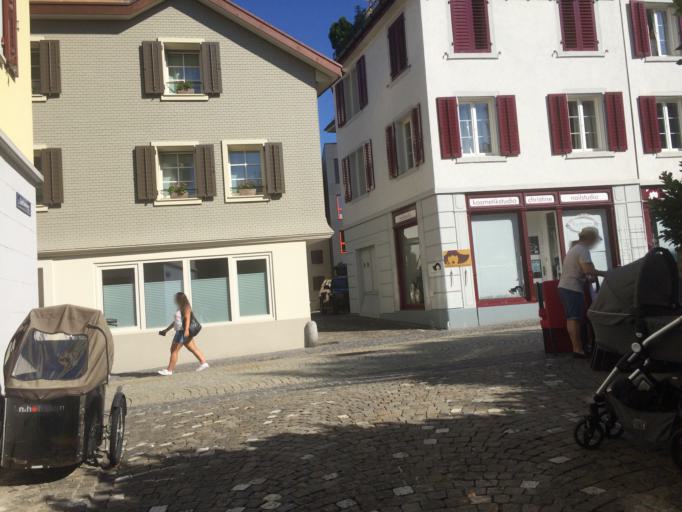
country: CH
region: Zurich
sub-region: Bezirk Horgen
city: Horgen
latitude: 47.2608
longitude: 8.5992
